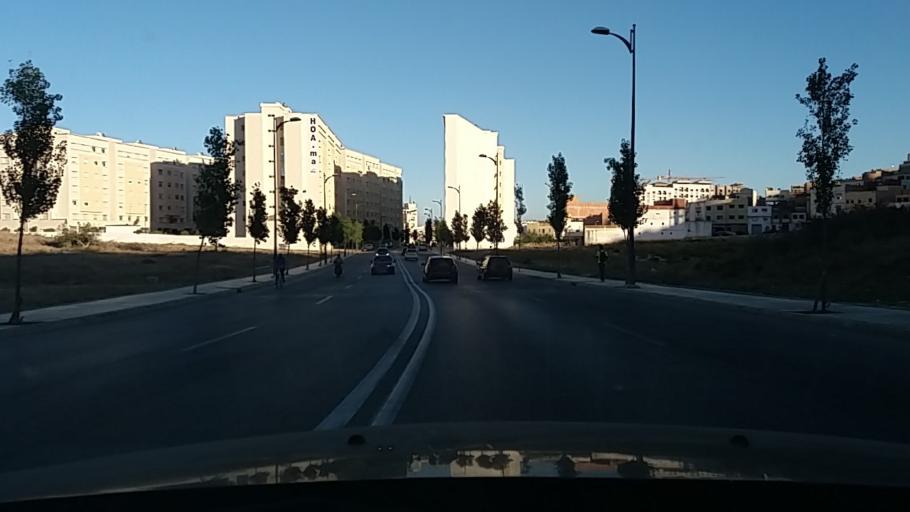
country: MA
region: Tanger-Tetouan
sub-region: Tanger-Assilah
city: Boukhalef
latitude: 35.7678
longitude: -5.8590
